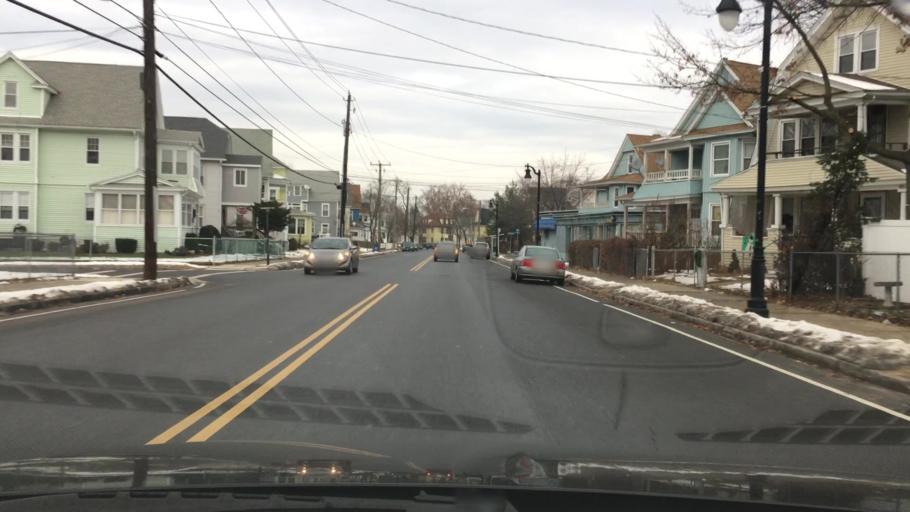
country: US
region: Massachusetts
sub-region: Hampden County
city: Springfield
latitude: 42.0812
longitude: -72.5545
